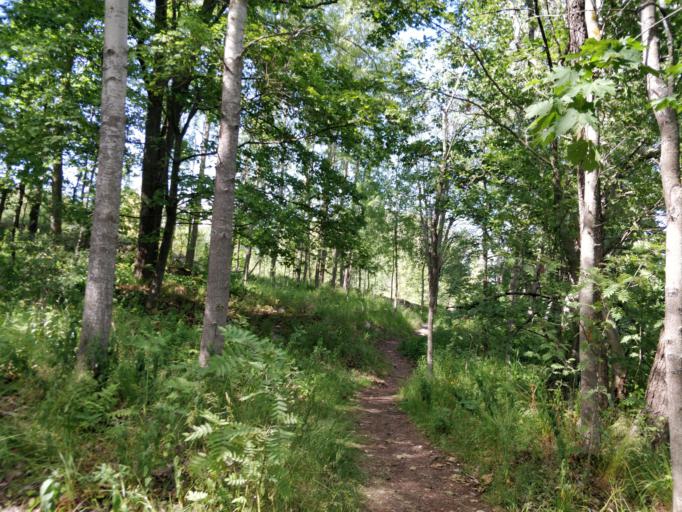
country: FI
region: Uusimaa
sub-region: Helsinki
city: Helsinki
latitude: 60.2031
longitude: 24.9957
